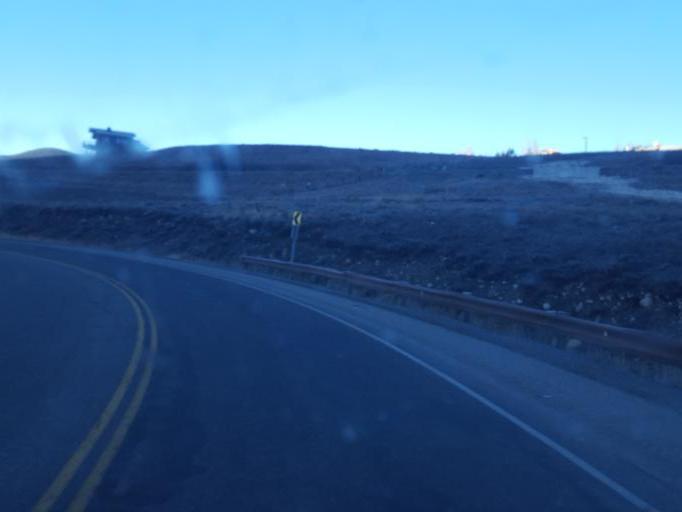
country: US
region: Colorado
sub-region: Gunnison County
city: Crested Butte
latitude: 38.8926
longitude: -106.9730
